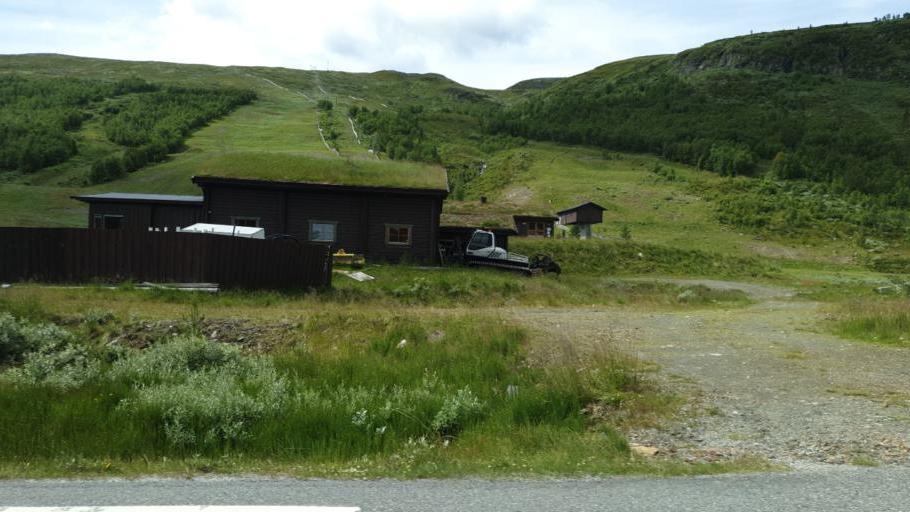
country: NO
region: Oppland
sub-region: Vaga
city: Vagamo
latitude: 61.7555
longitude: 9.0714
